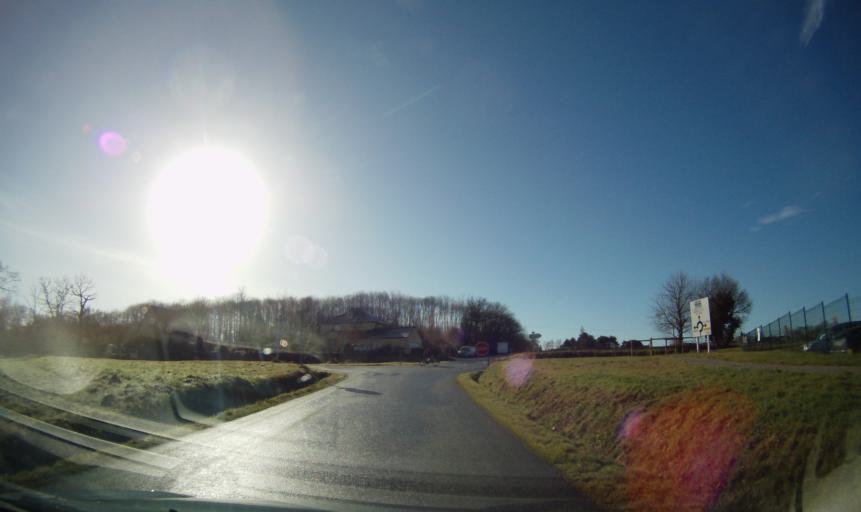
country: FR
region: Brittany
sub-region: Departement d'Ille-et-Vilaine
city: Crevin
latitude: 47.9316
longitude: -1.6668
